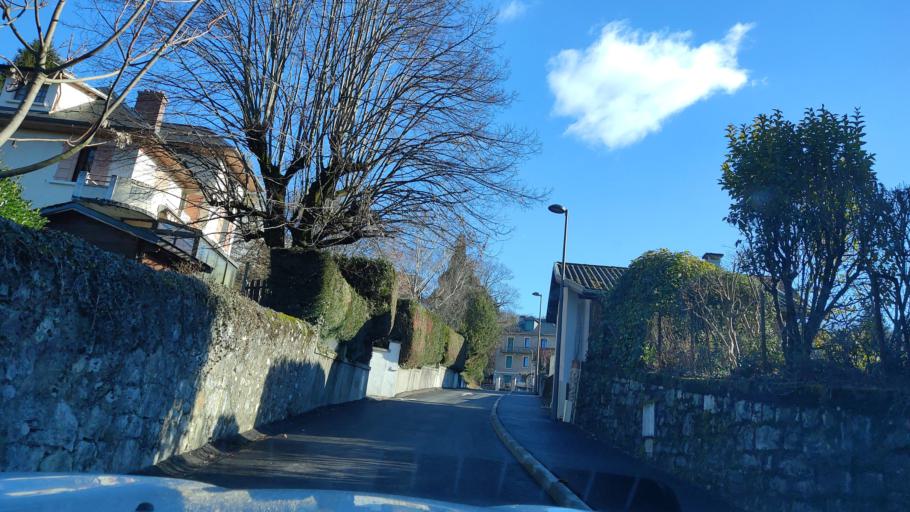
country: FR
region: Rhone-Alpes
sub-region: Departement de la Savoie
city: Jacob-Bellecombette
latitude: 45.5597
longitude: 5.9162
